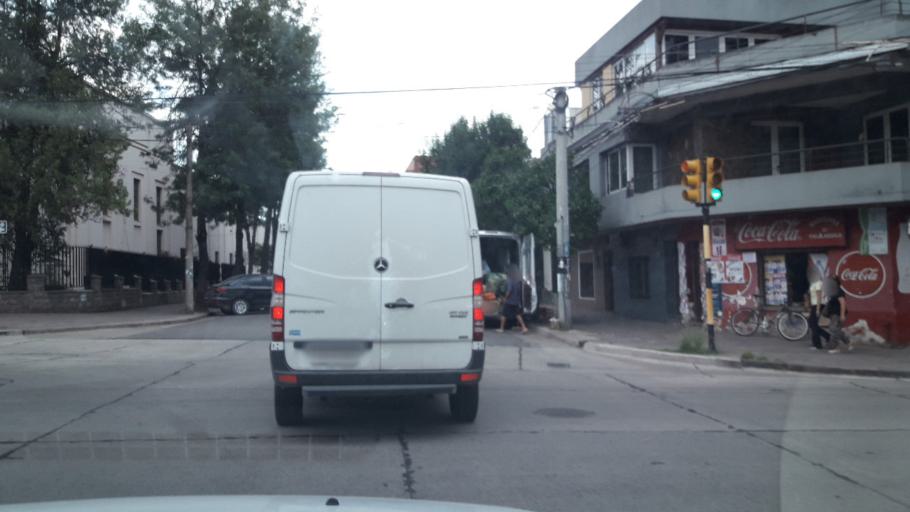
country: AR
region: Jujuy
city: San Salvador de Jujuy
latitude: -24.1822
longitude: -65.3128
